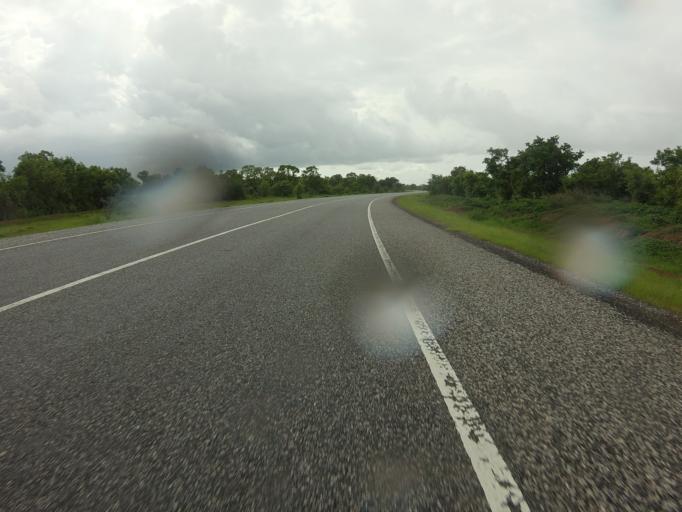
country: GH
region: Northern
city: Tamale
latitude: 9.1394
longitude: -1.3491
